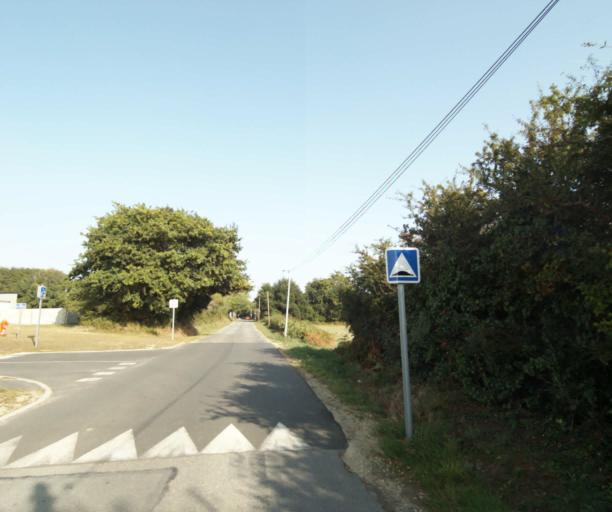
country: FR
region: Brittany
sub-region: Departement du Morbihan
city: Locmiquelic
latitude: 47.7210
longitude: -3.3297
